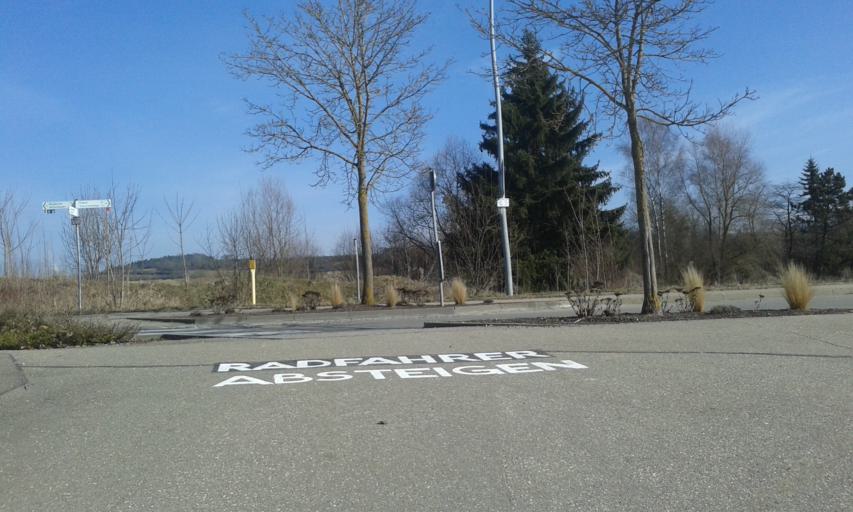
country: DE
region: Baden-Wuerttemberg
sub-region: Tuebingen Region
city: Ehingen
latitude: 48.2930
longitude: 9.7271
